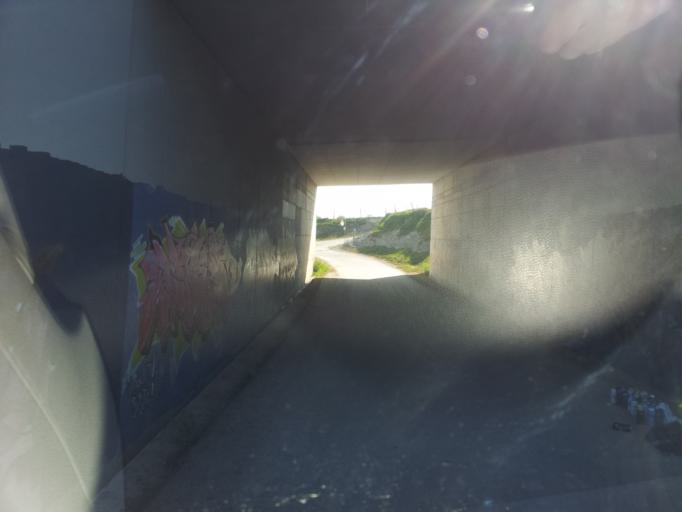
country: ES
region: Catalonia
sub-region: Provincia de Barcelona
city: Gurb
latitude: 41.9365
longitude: 2.2201
